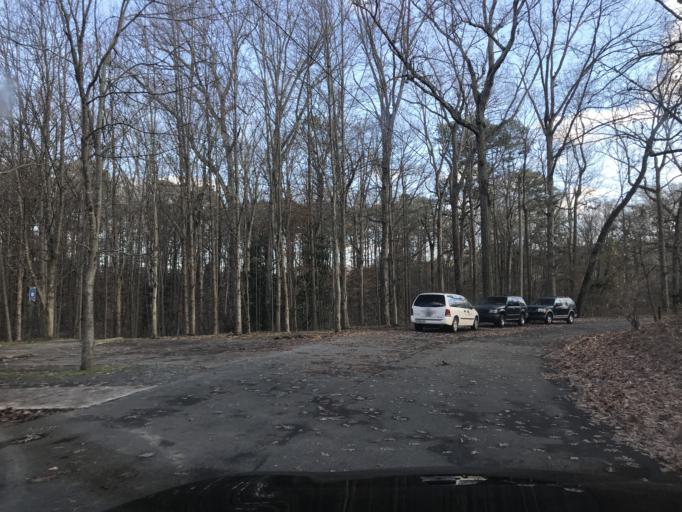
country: US
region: Georgia
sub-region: Fulton County
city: College Park
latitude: 33.6392
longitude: -84.4705
